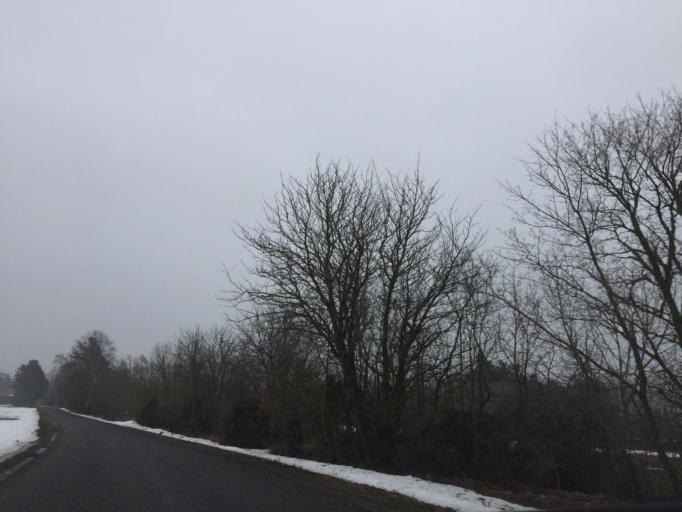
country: EE
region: Saare
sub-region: Kuressaare linn
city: Kuressaare
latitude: 58.2722
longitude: 22.5777
